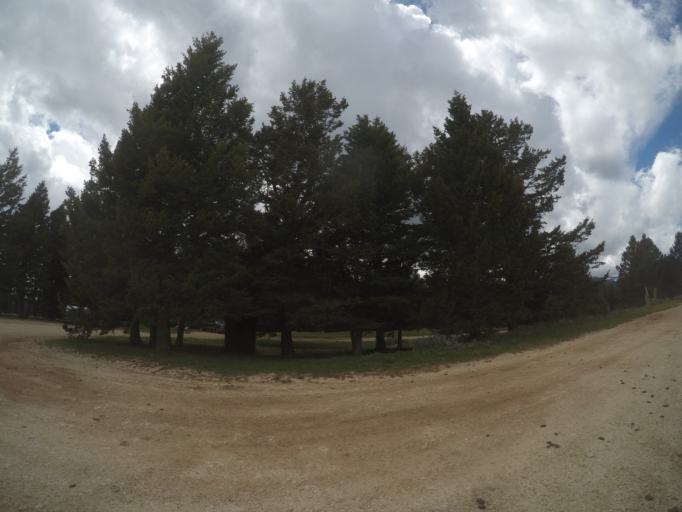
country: US
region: Wyoming
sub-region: Big Horn County
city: Lovell
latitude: 45.1619
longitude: -108.4014
